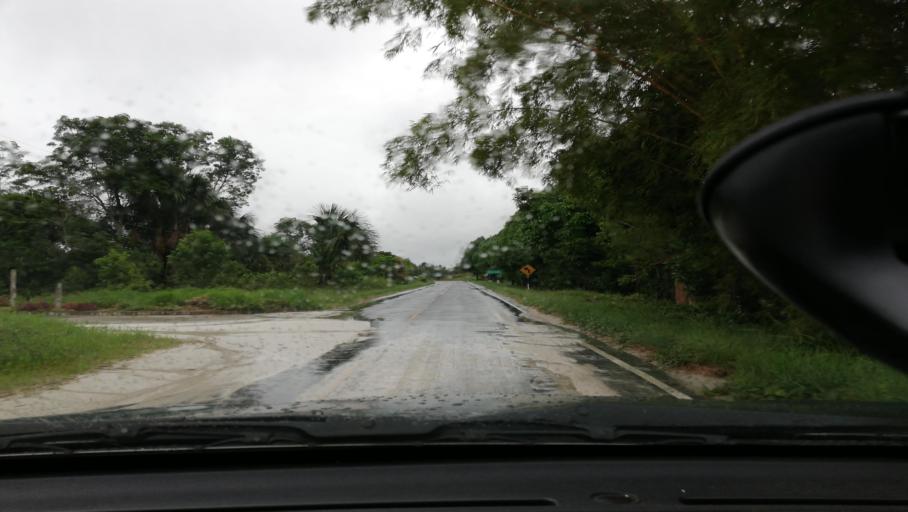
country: PE
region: Loreto
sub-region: Provincia de Maynas
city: San Juan
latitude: -4.1576
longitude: -73.4734
